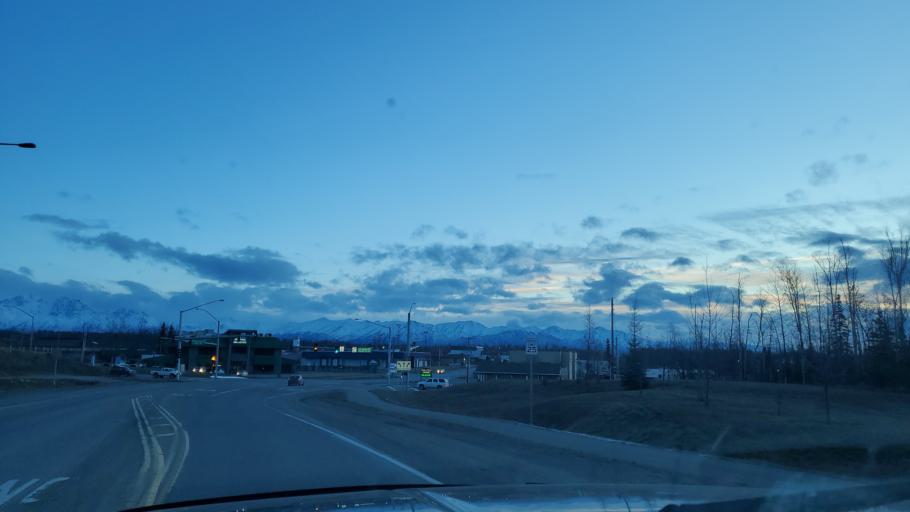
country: US
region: Alaska
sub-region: Matanuska-Susitna Borough
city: Wasilla
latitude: 61.5860
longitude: -149.4428
